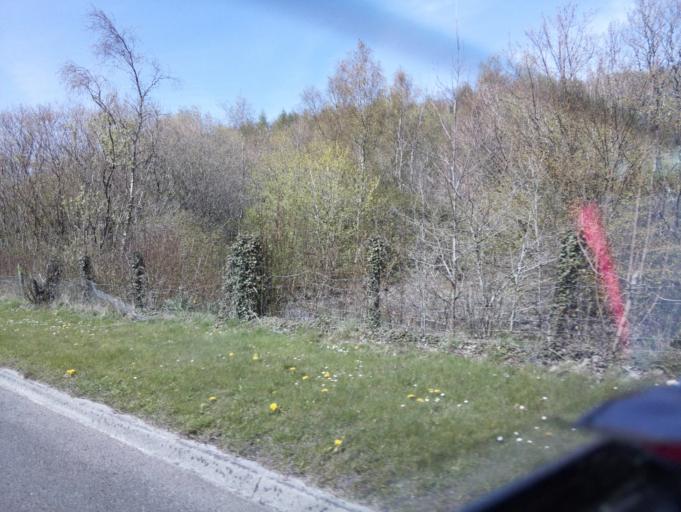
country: GB
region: Wales
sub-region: Rhondda Cynon Taf
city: Mountain Ash
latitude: 51.6890
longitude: -3.3949
